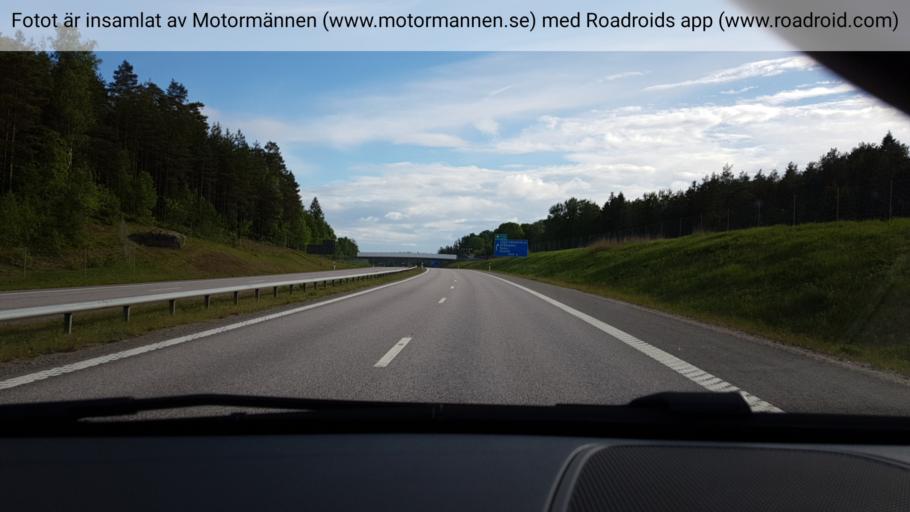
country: SE
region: Stockholm
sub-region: Nynashamns Kommun
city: Osmo
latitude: 58.9858
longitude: 17.9205
